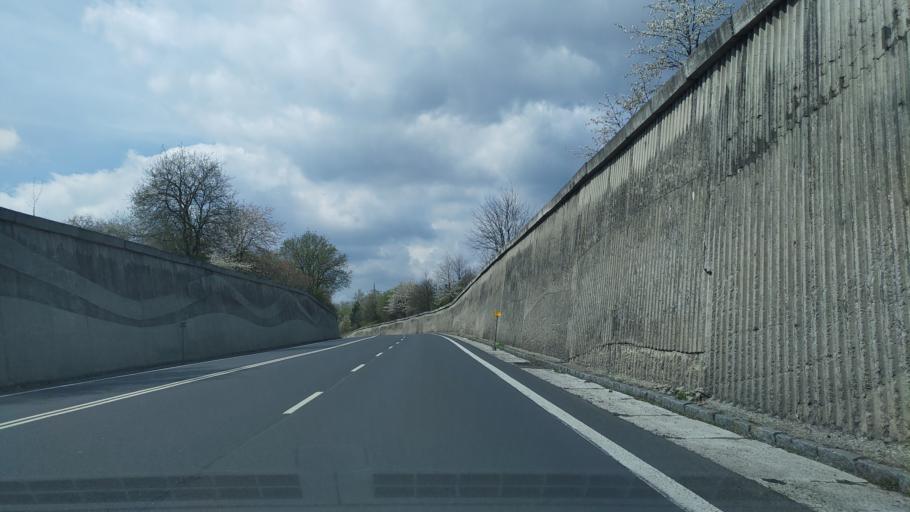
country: CZ
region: Ustecky
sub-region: Okres Chomutov
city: Klasterec nad Ohri
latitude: 50.3849
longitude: 13.1510
